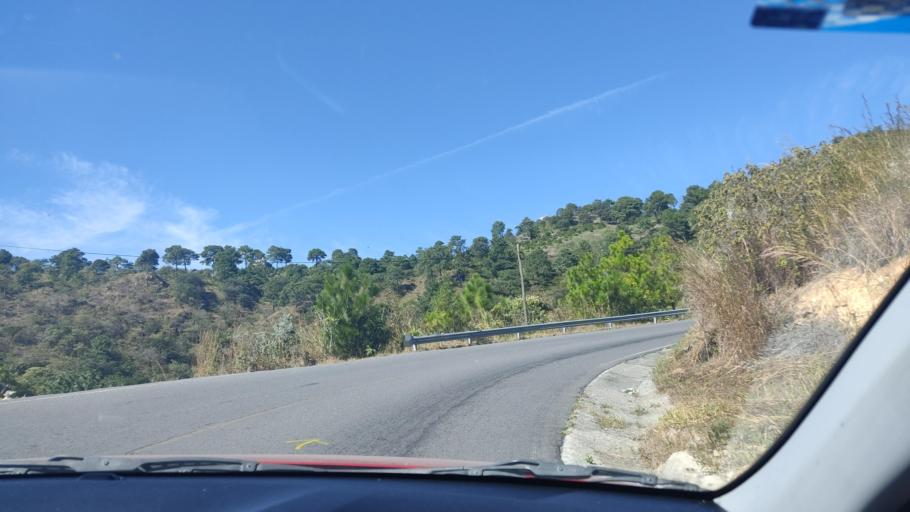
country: MX
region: Nayarit
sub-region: Jala
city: Rosa Blanca
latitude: 21.0938
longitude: -104.3827
